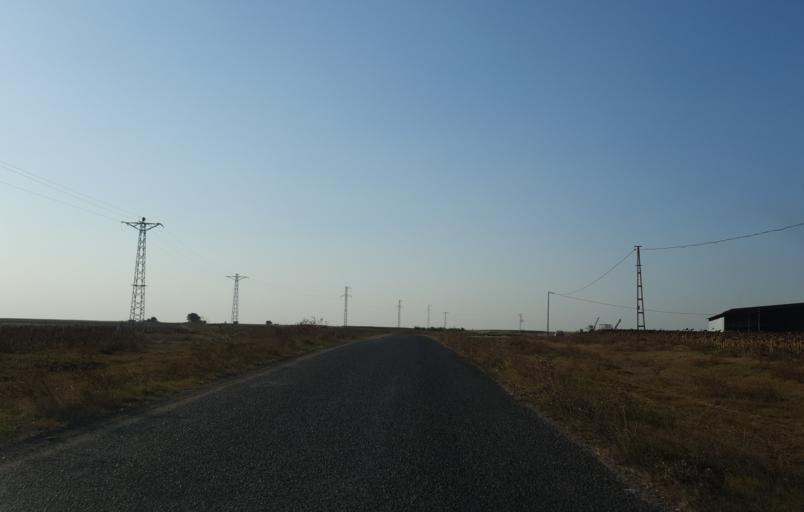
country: TR
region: Tekirdag
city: Beyazkoy
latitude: 41.3981
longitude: 27.7615
